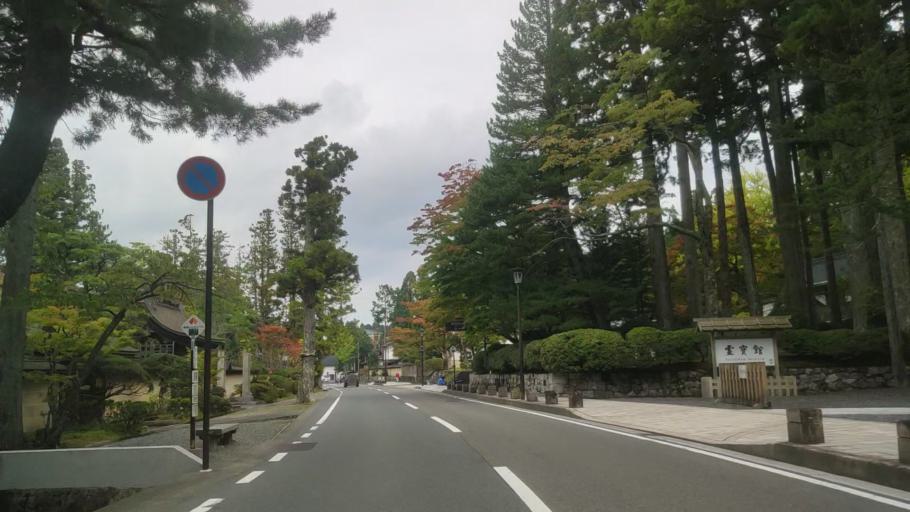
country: JP
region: Wakayama
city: Koya
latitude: 34.2121
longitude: 135.5811
